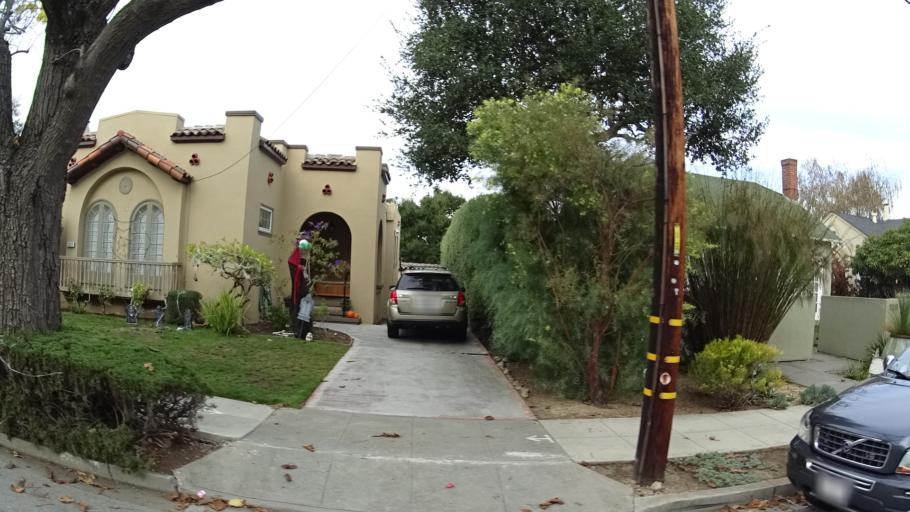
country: US
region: California
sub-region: San Mateo County
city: Burlingame
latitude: 37.5803
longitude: -122.3703
